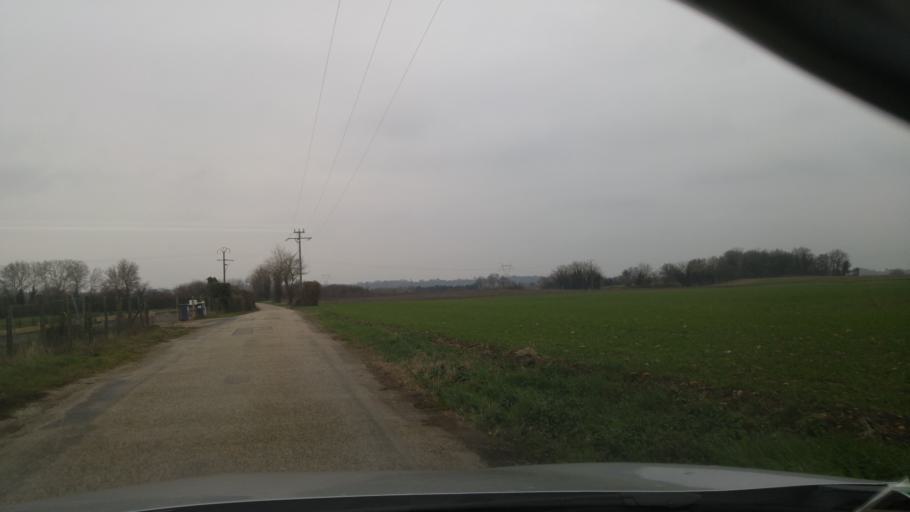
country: FR
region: Rhone-Alpes
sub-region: Departement de l'Isere
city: Charvieu-Chavagneux
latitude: 45.7266
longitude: 5.1423
